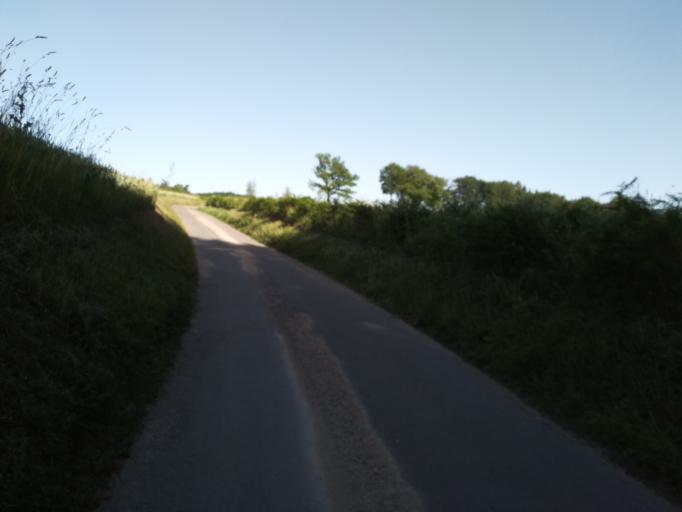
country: FR
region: Bourgogne
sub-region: Departement de la Cote-d'Or
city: Saulieu
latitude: 47.2839
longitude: 4.1476
